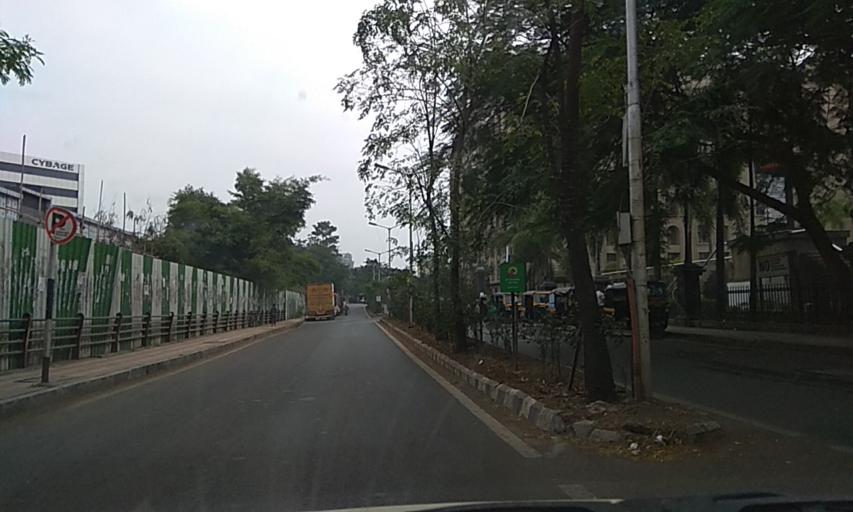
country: IN
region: Maharashtra
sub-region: Pune Division
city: Lohogaon
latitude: 18.5454
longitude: 73.9099
